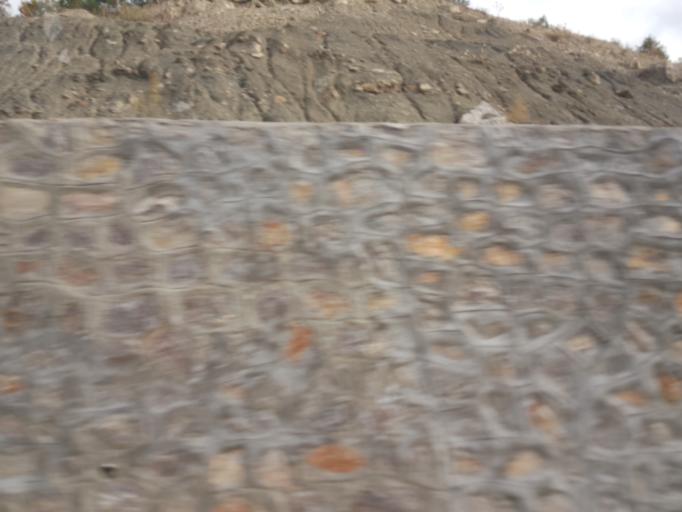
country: TR
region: Sinop
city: Duragan
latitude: 41.4578
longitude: 35.0424
